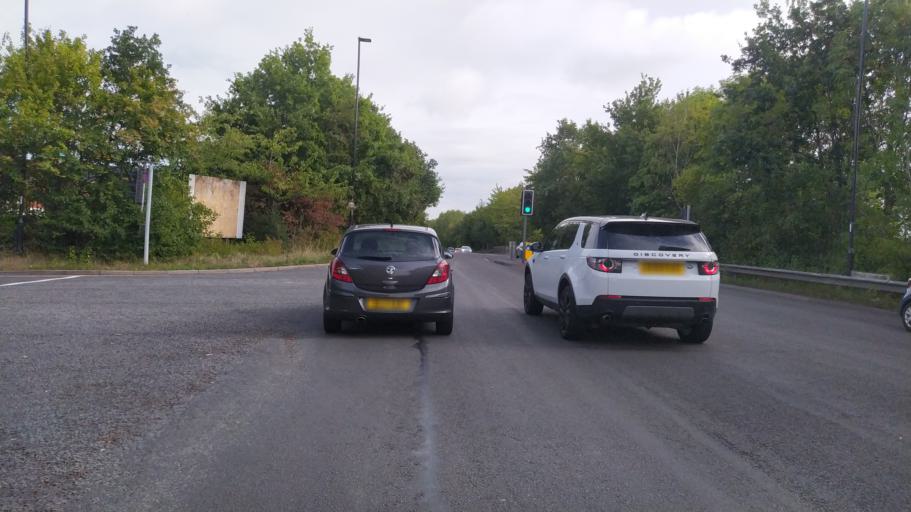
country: GB
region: England
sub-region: Southampton
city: Southampton
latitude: 50.9285
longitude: -1.3847
